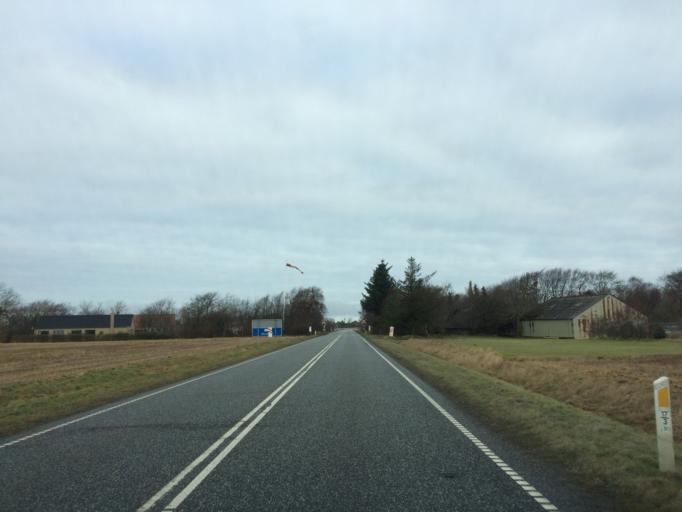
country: DK
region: Central Jutland
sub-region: Holstebro Kommune
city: Ulfborg
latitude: 56.3675
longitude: 8.4399
